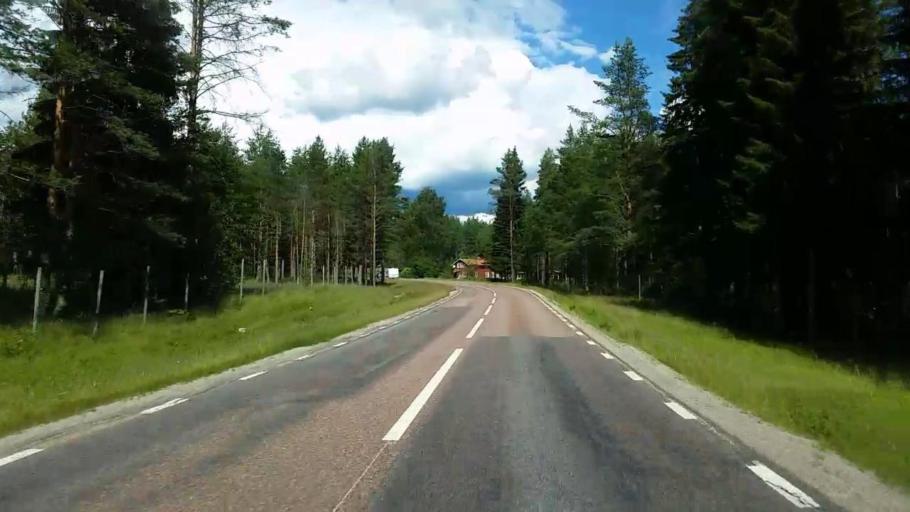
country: SE
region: Gaevleborg
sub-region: Ovanakers Kommun
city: Edsbyn
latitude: 61.3038
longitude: 15.5092
